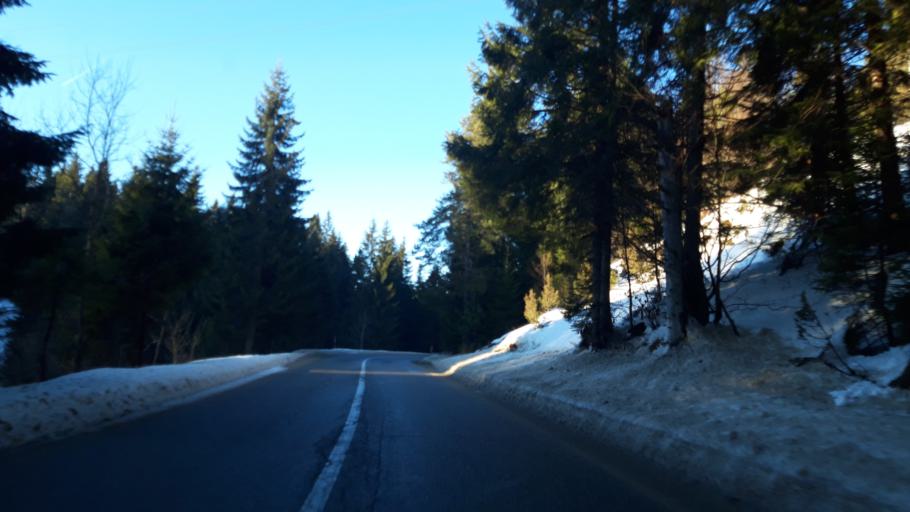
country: BA
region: Republika Srpska
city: Han Pijesak
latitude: 44.1183
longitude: 18.9699
